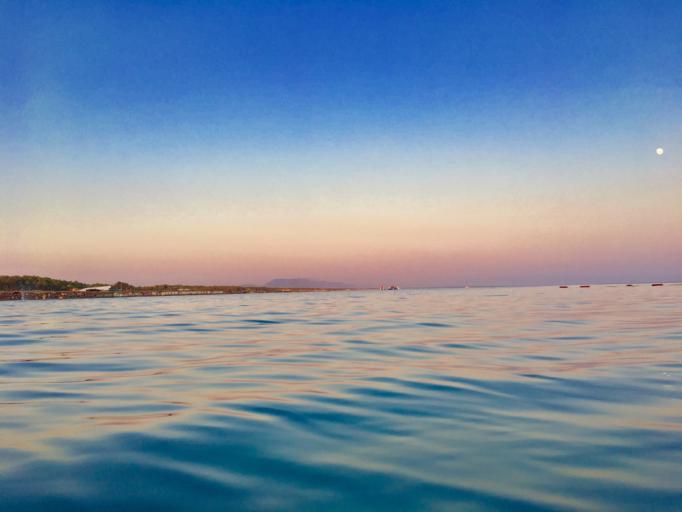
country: ME
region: Ulcinj
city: Ulcinj
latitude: 41.9085
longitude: 19.2392
